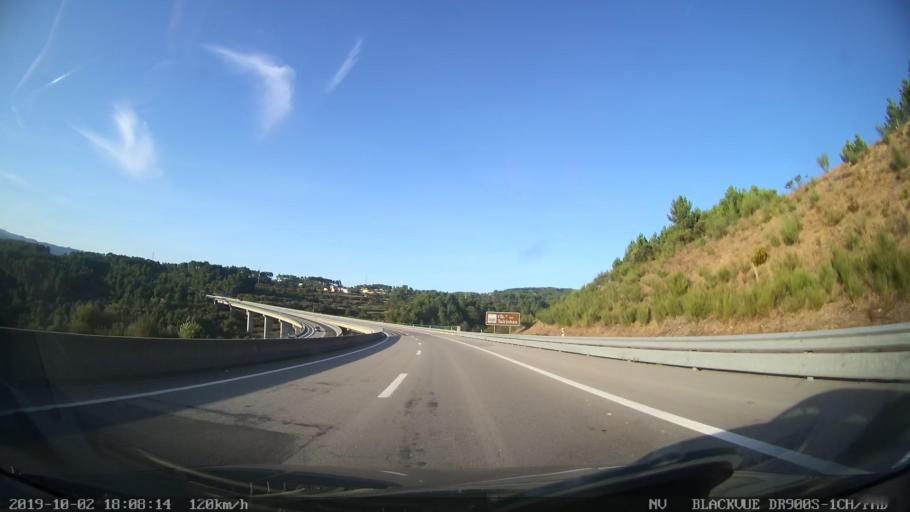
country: PT
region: Vila Real
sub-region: Vila Real
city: Vila Real
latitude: 41.3065
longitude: -7.6865
